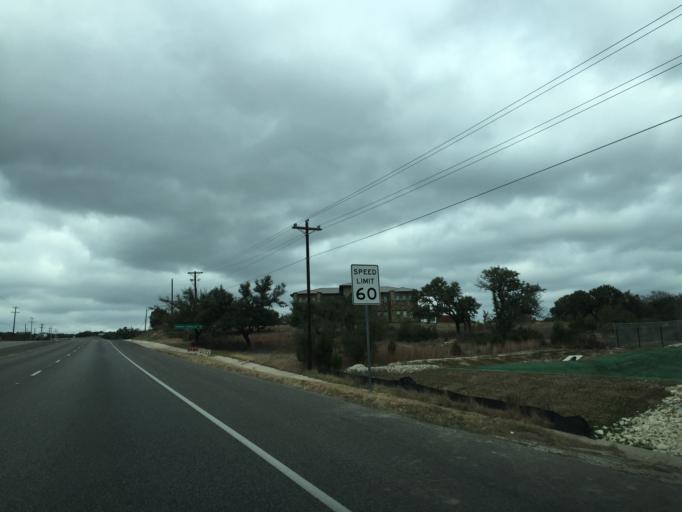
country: US
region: Texas
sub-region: Travis County
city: The Hills
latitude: 30.3427
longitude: -98.0450
